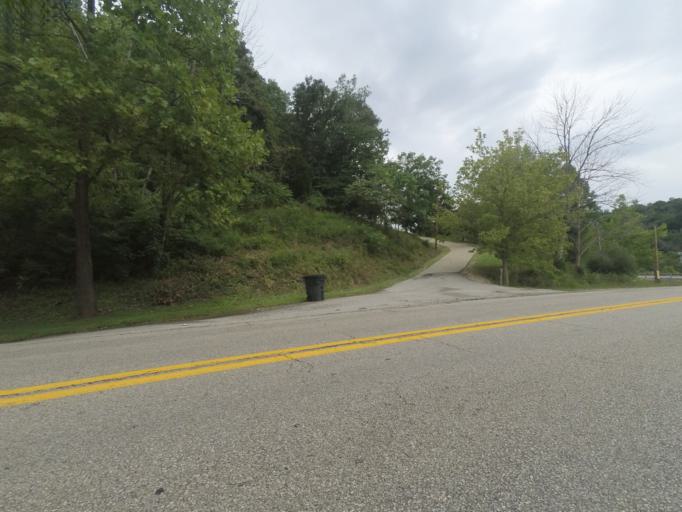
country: US
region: West Virginia
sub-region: Cabell County
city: Huntington
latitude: 38.3949
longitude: -82.4557
